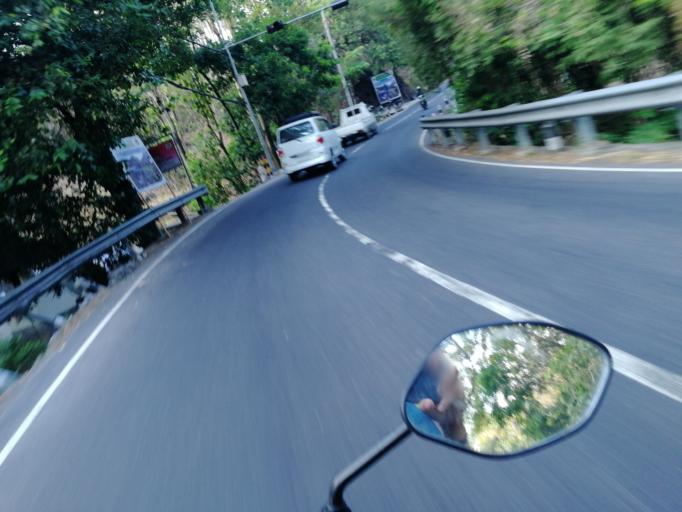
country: ID
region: Bali
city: Banjar Kangkaang
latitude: -8.3538
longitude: 115.6131
